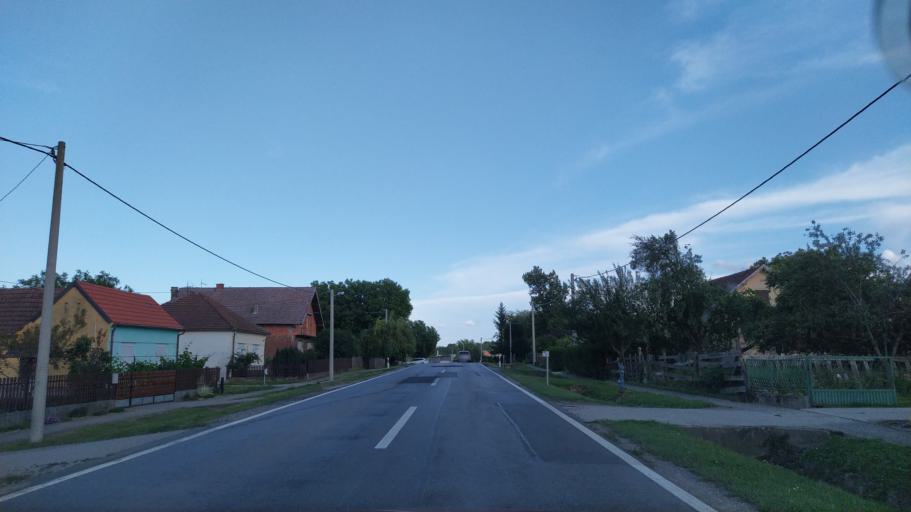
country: HR
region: Virovitick-Podravska
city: Slatina
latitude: 45.7283
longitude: 17.6305
